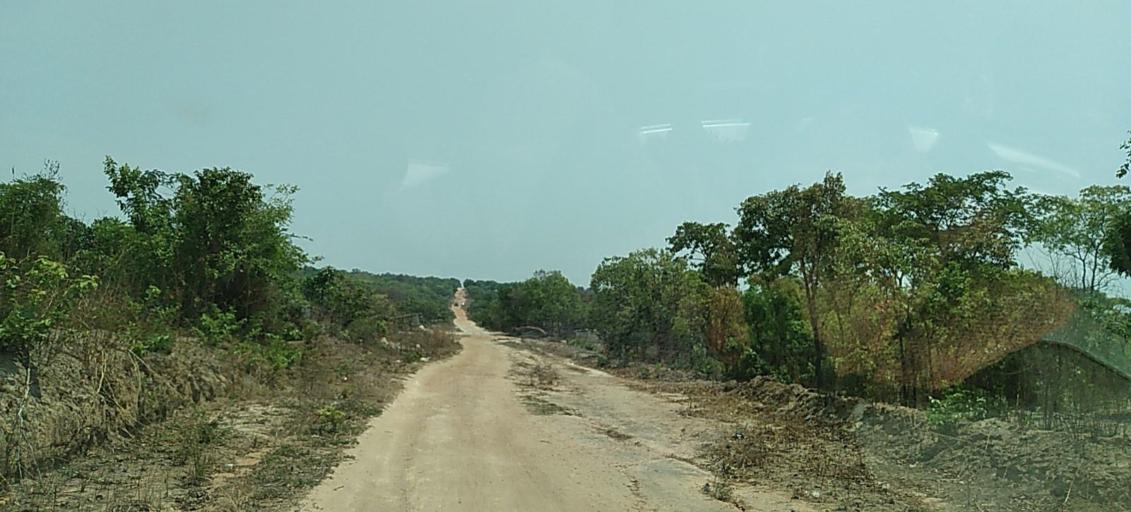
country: ZM
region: Copperbelt
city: Kalulushi
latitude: -12.9348
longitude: 28.1628
